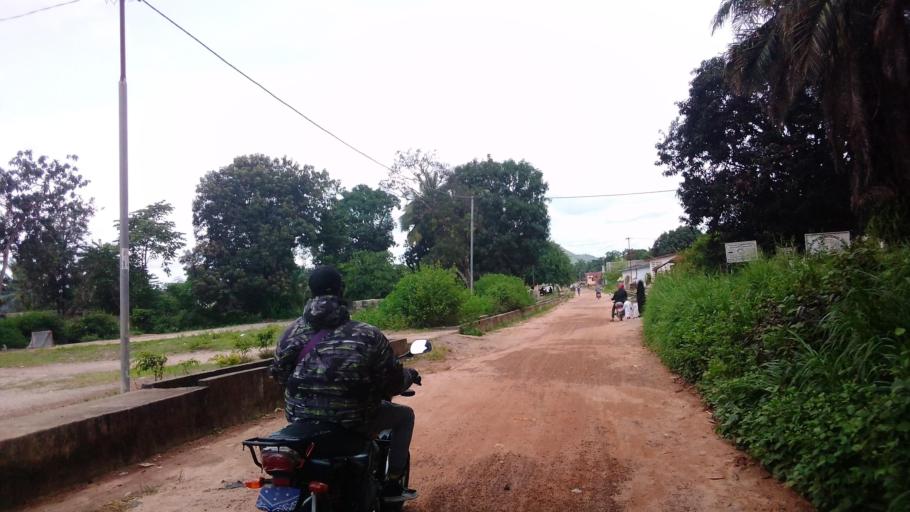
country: SL
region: Northern Province
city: Makeni
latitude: 8.8745
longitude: -12.0374
